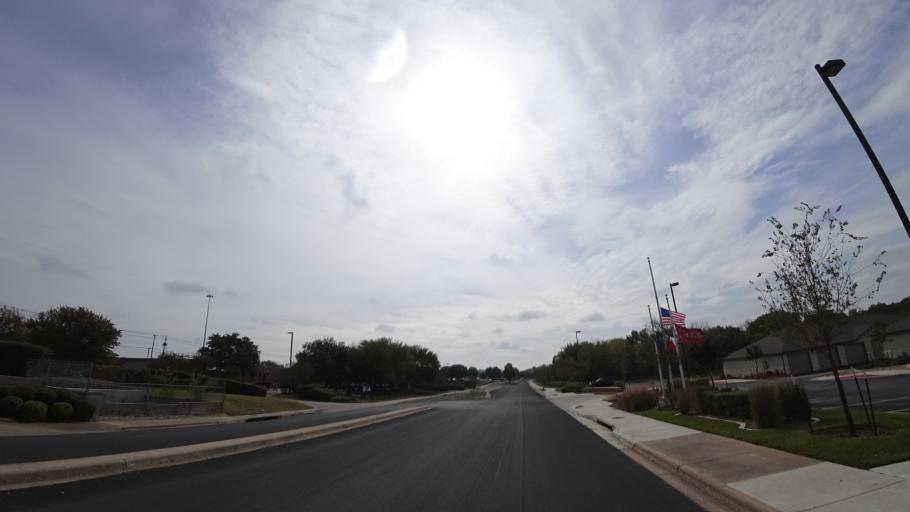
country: US
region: Texas
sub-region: Travis County
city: Wells Branch
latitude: 30.4358
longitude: -97.6710
